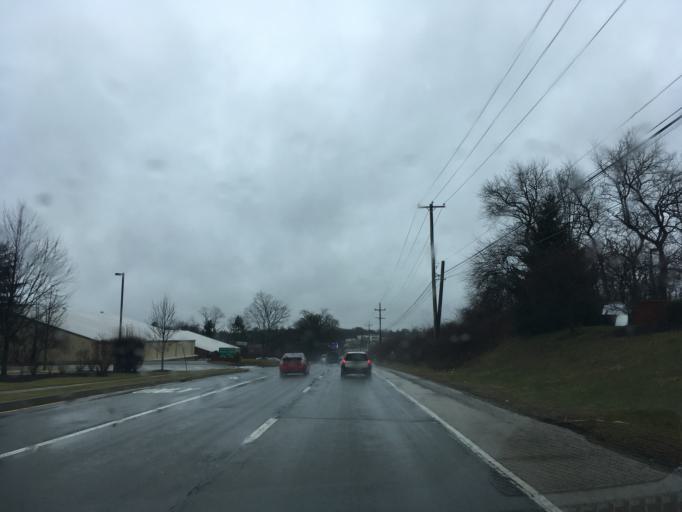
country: US
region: Pennsylvania
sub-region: Delaware County
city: Chester Heights
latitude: 39.8592
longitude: -75.5420
